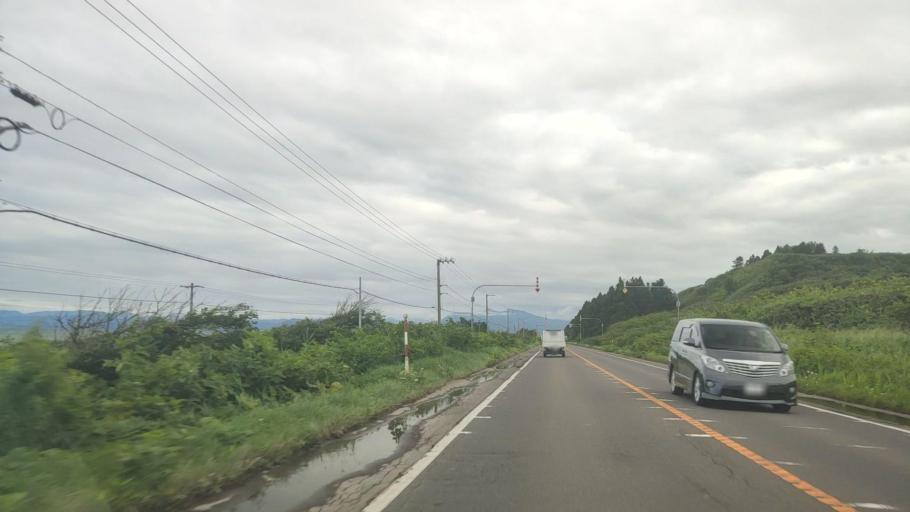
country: JP
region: Hokkaido
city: Niseko Town
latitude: 42.3454
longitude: 140.2821
